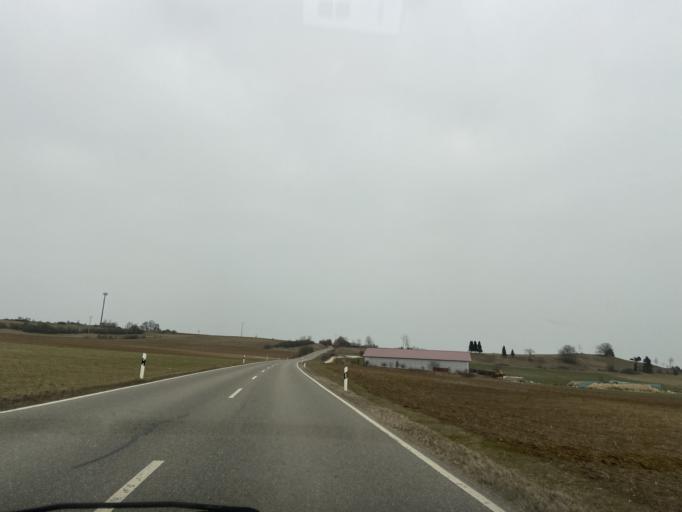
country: DE
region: Baden-Wuerttemberg
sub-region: Tuebingen Region
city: Hettingen
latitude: 48.1786
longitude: 9.2682
